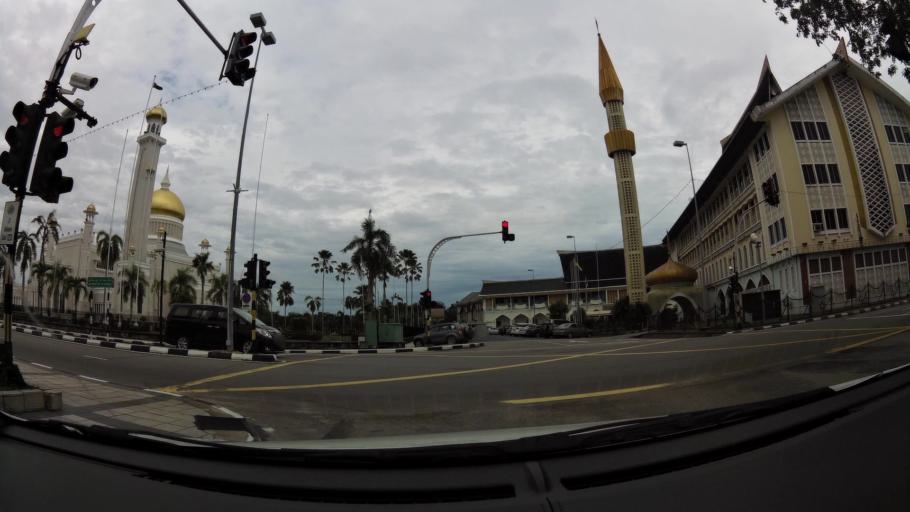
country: BN
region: Brunei and Muara
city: Bandar Seri Begawan
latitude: 4.8902
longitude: 114.9401
